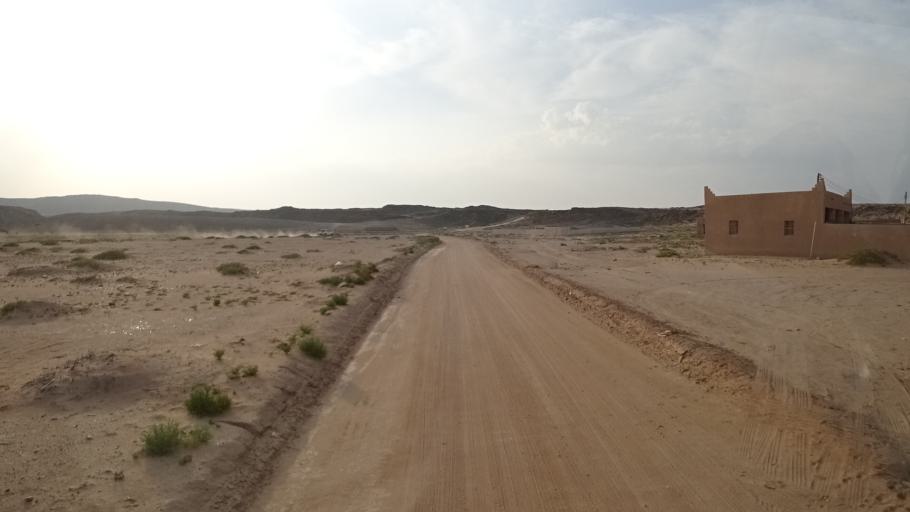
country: OM
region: Ash Sharqiyah
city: Sur
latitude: 22.4493
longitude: 59.8271
